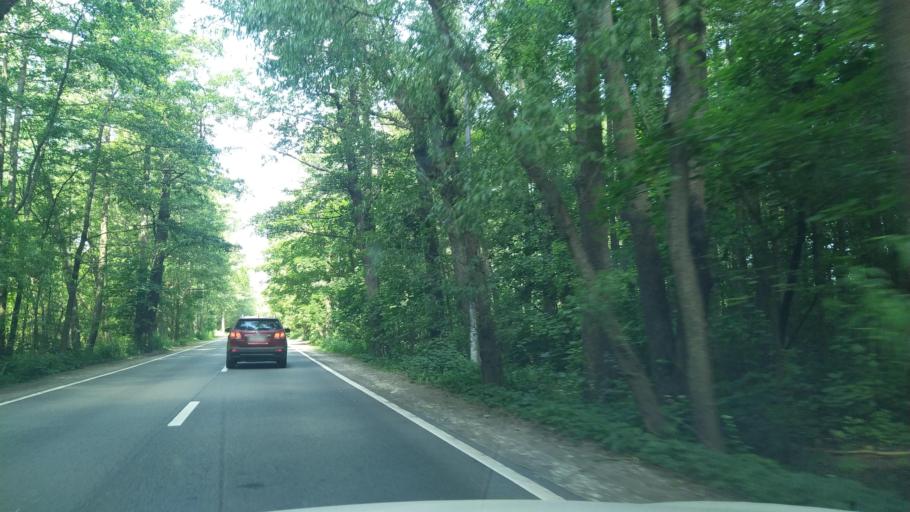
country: RU
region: St.-Petersburg
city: Kronshtadt
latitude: 60.0219
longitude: 29.6924
